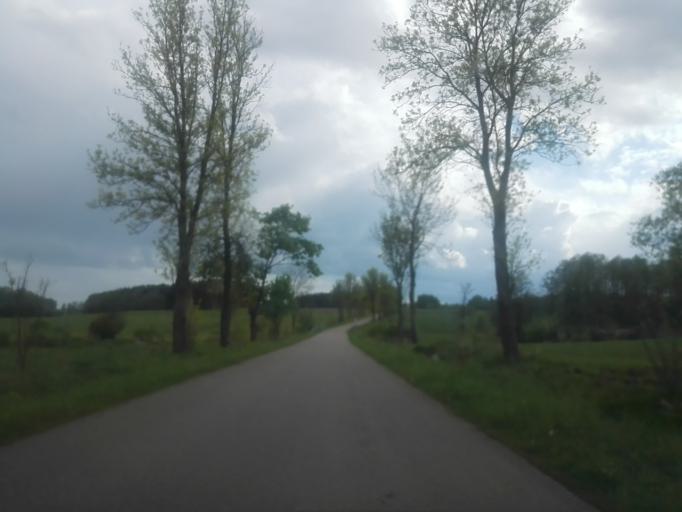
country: PL
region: Podlasie
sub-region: Powiat lomzynski
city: Wizna
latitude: 53.2711
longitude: 22.4528
